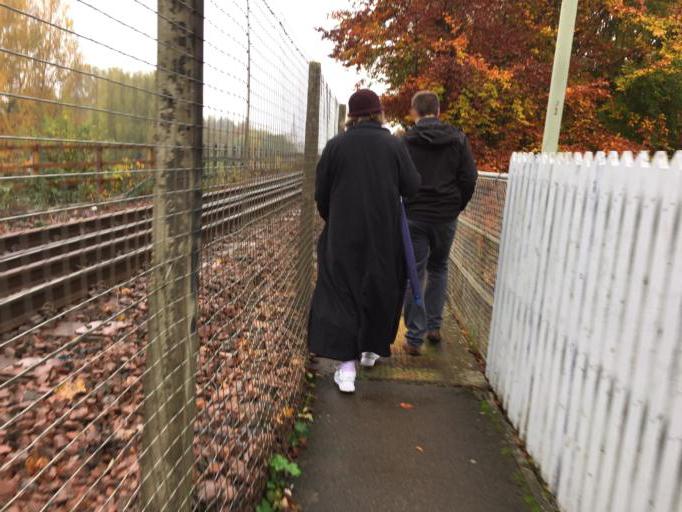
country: GB
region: Scotland
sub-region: Perth and Kinross
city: Perth
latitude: 56.3900
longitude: -3.4211
